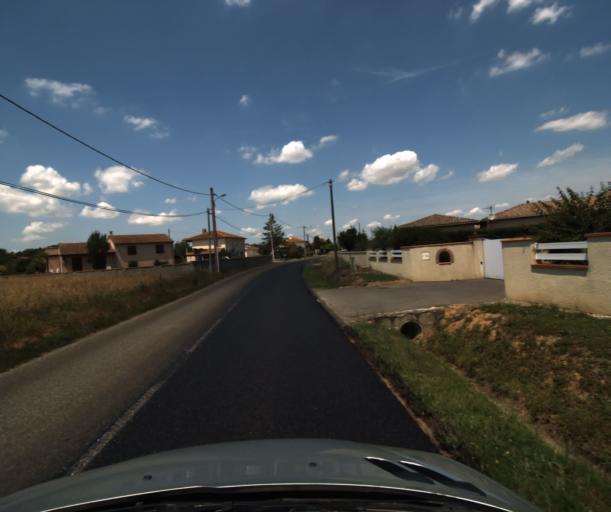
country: FR
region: Midi-Pyrenees
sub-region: Departement de la Haute-Garonne
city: Saint-Lys
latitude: 43.5005
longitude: 1.1952
